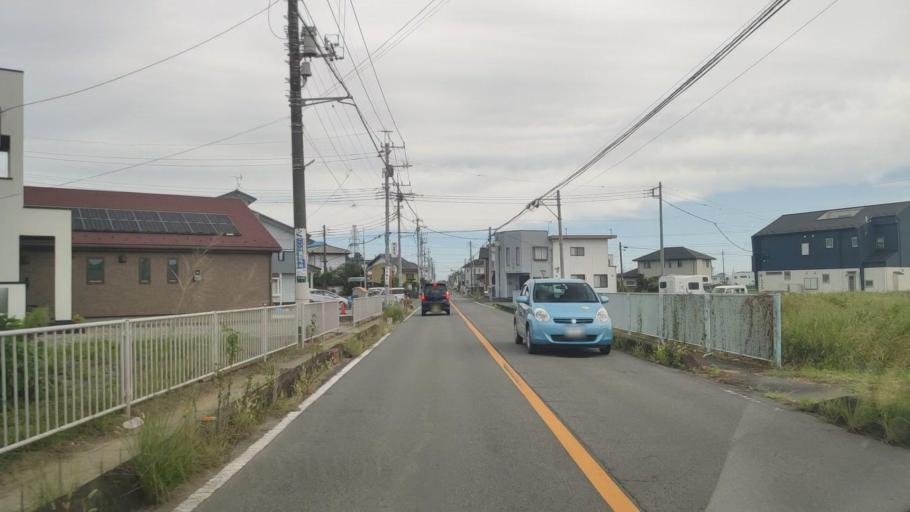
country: JP
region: Gunma
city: Takasaki
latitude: 36.3618
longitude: 138.9811
